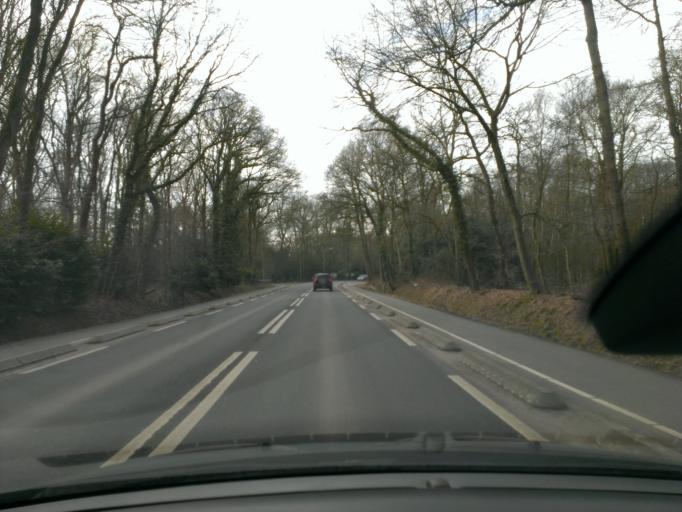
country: NL
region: Gelderland
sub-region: Gemeente Epe
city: Epe
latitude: 52.3631
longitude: 6.0078
